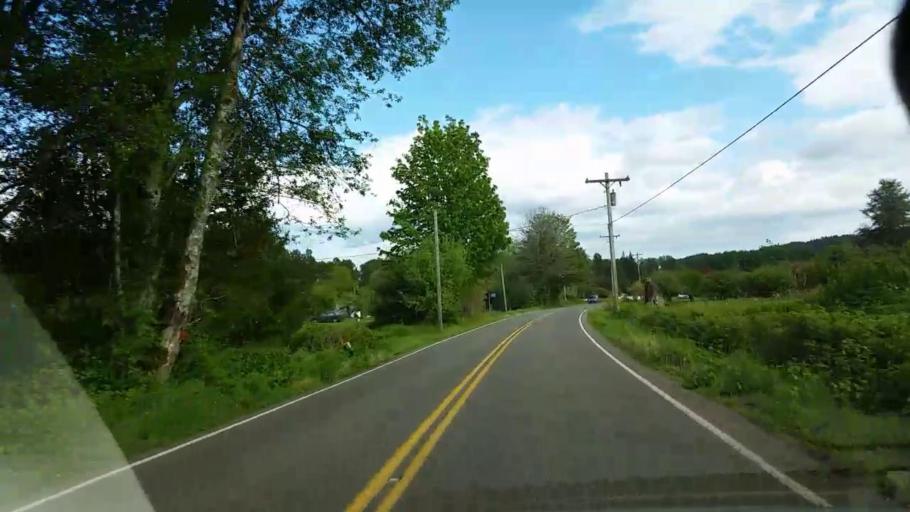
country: US
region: Washington
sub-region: Mason County
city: Shelton
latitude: 47.3200
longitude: -123.2642
